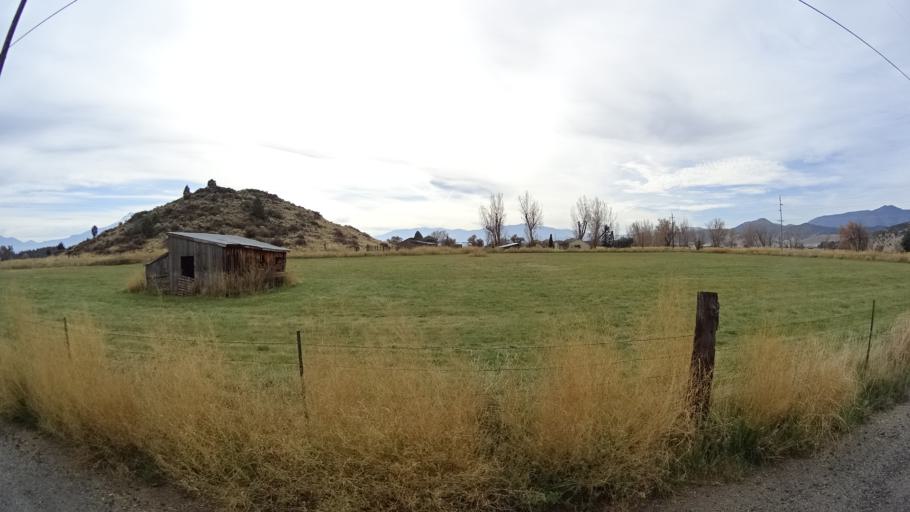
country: US
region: California
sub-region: Siskiyou County
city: Montague
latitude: 41.6580
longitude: -122.5189
